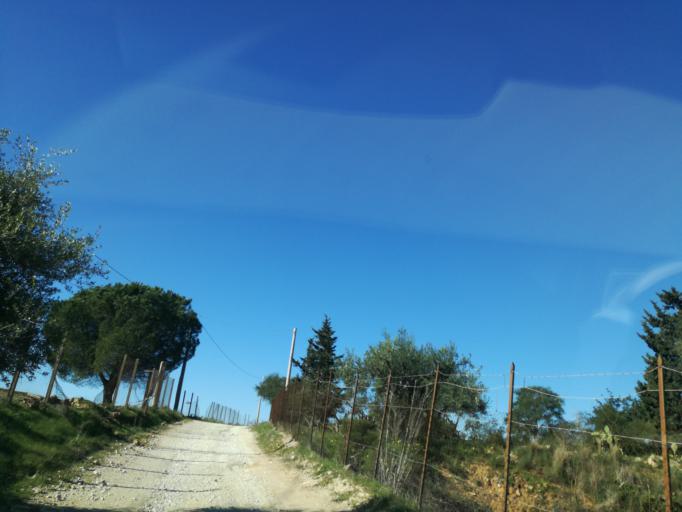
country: IT
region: Sicily
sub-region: Provincia di Caltanissetta
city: Niscemi
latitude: 37.0574
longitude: 14.3601
